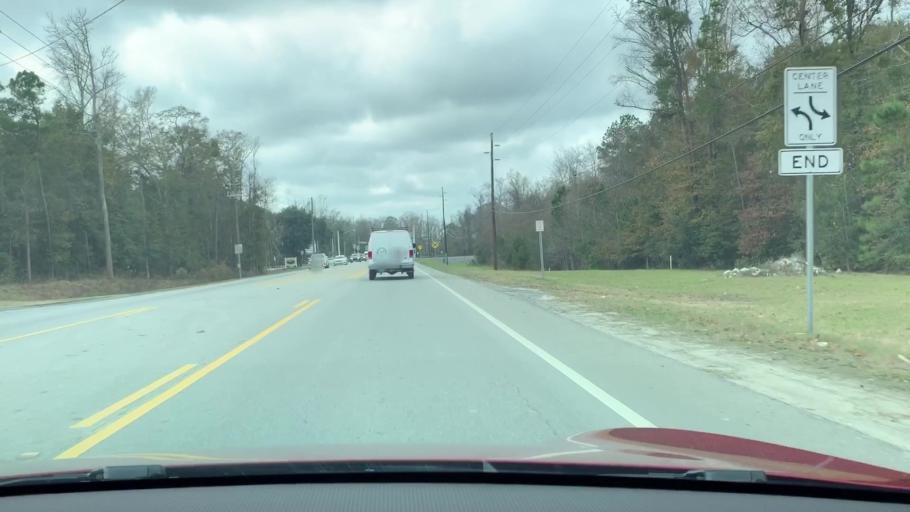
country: US
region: Georgia
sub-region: Chatham County
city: Port Wentworth
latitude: 32.1432
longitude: -81.1893
